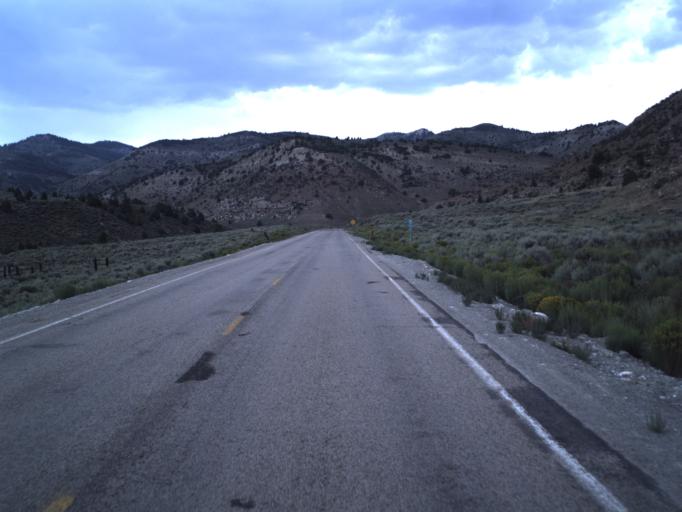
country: US
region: Utah
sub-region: Carbon County
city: Helper
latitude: 39.8227
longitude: -110.7851
